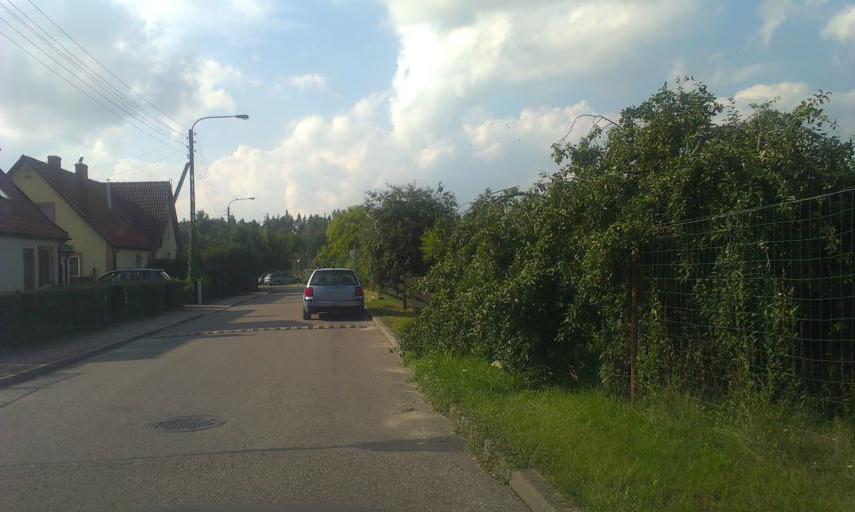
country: PL
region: West Pomeranian Voivodeship
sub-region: Powiat szczecinecki
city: Szczecinek
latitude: 53.7063
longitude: 16.7151
